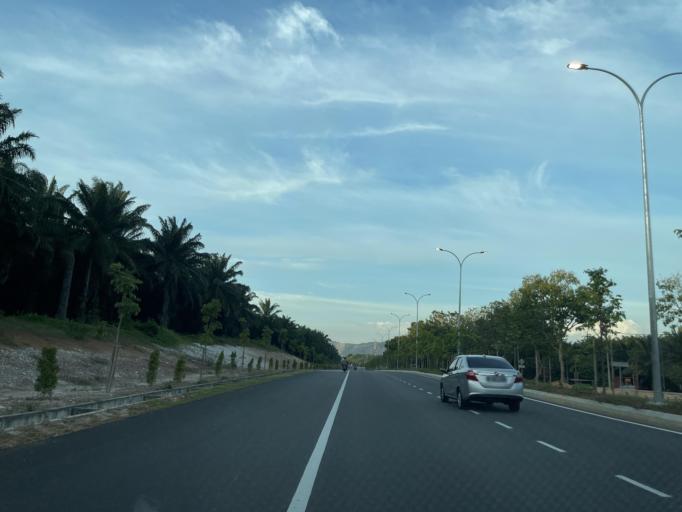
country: MY
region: Melaka
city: Kampung Ayer Keroh
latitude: 2.3202
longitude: 102.2489
